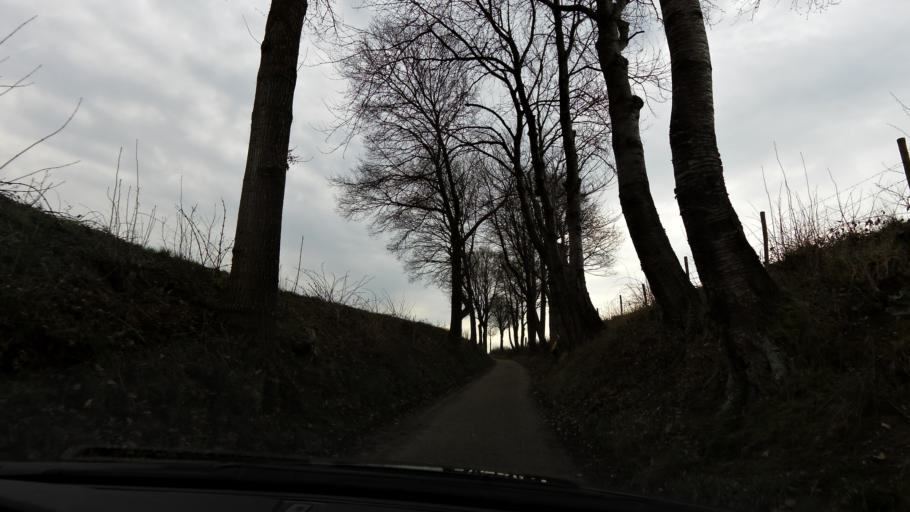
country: NL
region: Limburg
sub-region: Gemeente Simpelveld
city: Simpelveld
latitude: 50.8129
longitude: 6.0070
